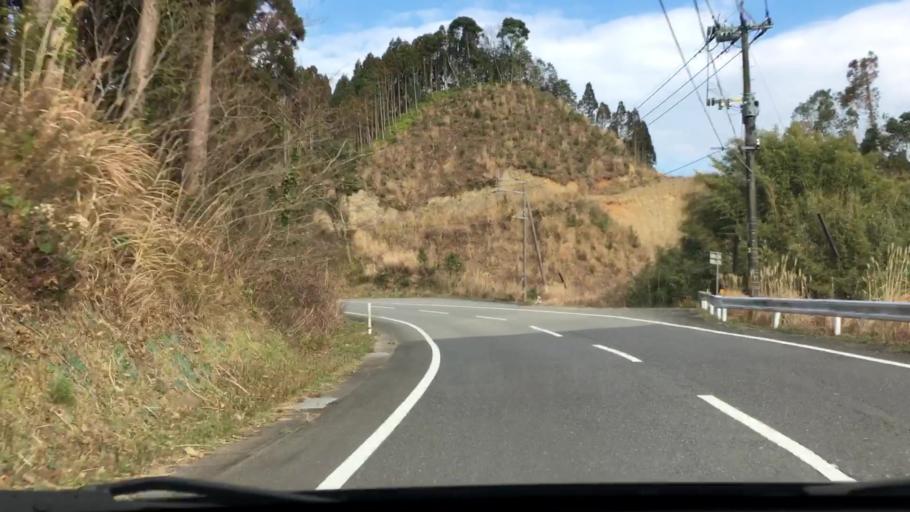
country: JP
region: Miyazaki
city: Kushima
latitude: 31.5753
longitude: 131.2680
